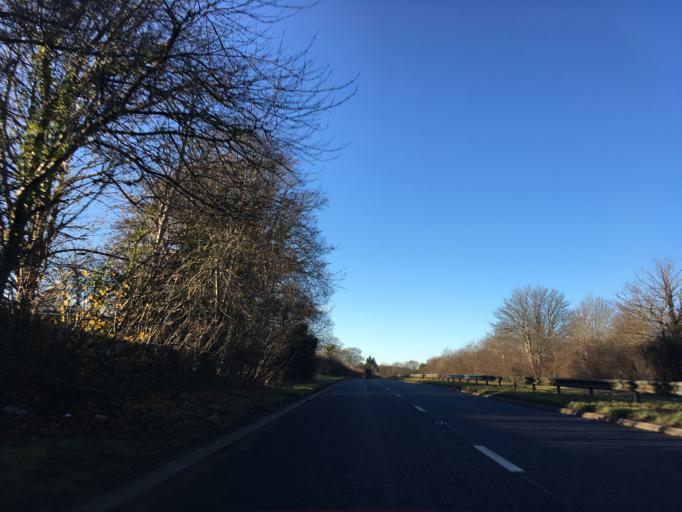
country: GB
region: England
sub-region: Bath and North East Somerset
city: Keynsham
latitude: 51.4143
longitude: -2.4892
